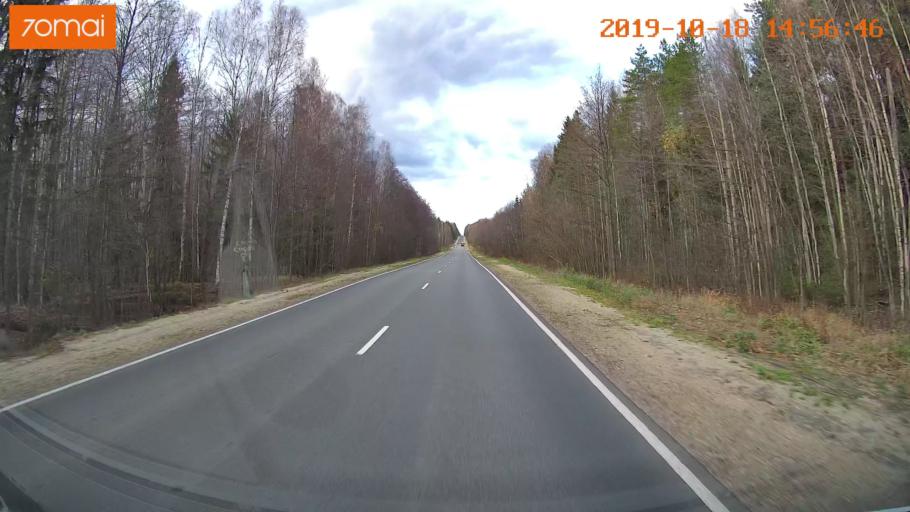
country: RU
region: Vladimir
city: Kurlovo
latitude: 55.4696
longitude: 40.5855
